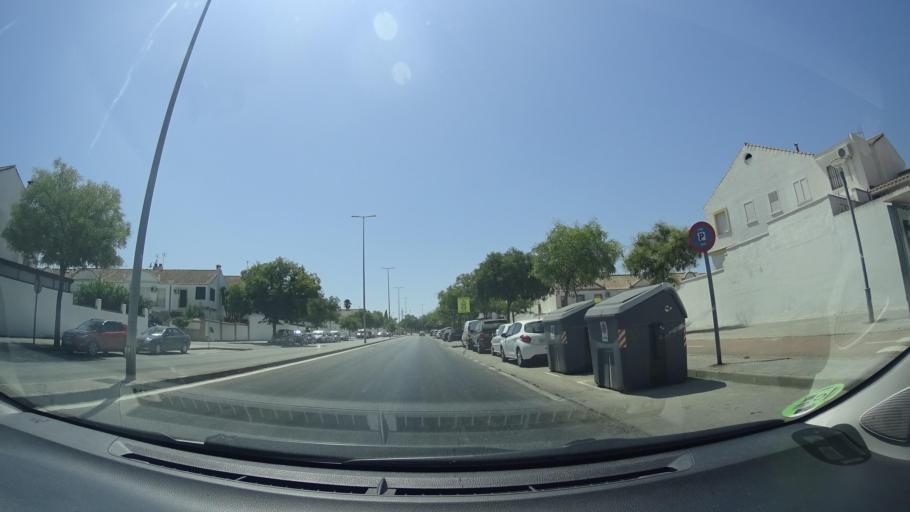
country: ES
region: Andalusia
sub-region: Provincia de Cadiz
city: Jerez de la Frontera
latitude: 36.6737
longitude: -6.1193
